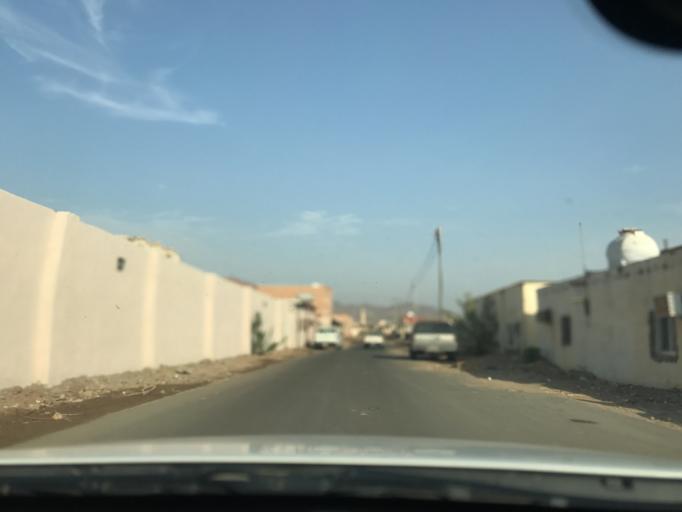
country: SA
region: Makkah
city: Al Jumum
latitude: 21.4426
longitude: 39.5192
